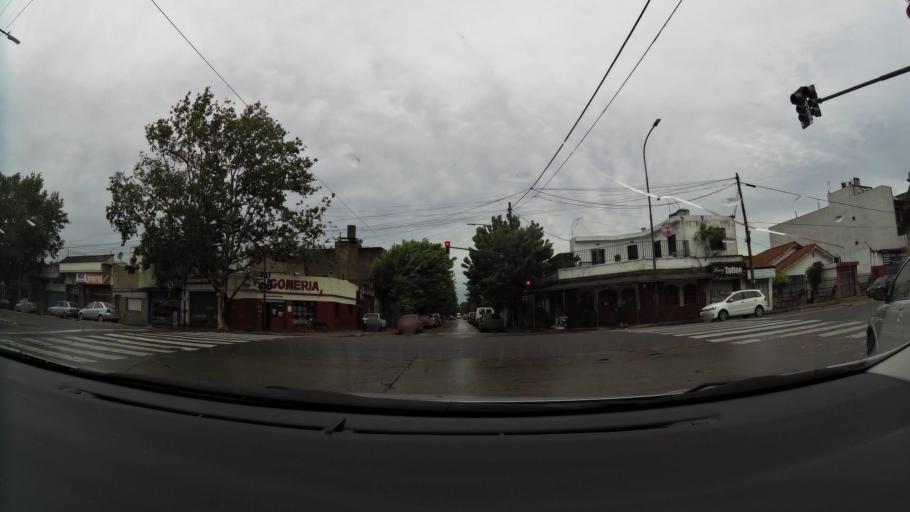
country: AR
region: Buenos Aires F.D.
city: Villa Lugano
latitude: -34.6609
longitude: -58.4447
